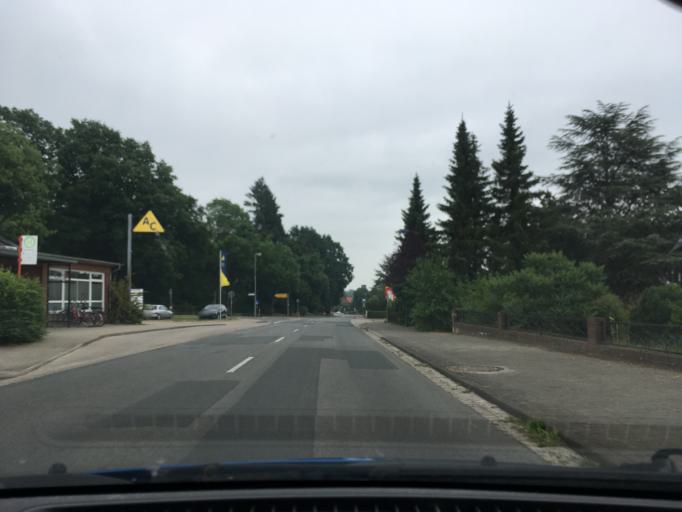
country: DE
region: Lower Saxony
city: Dahlenburg
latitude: 53.1888
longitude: 10.7308
